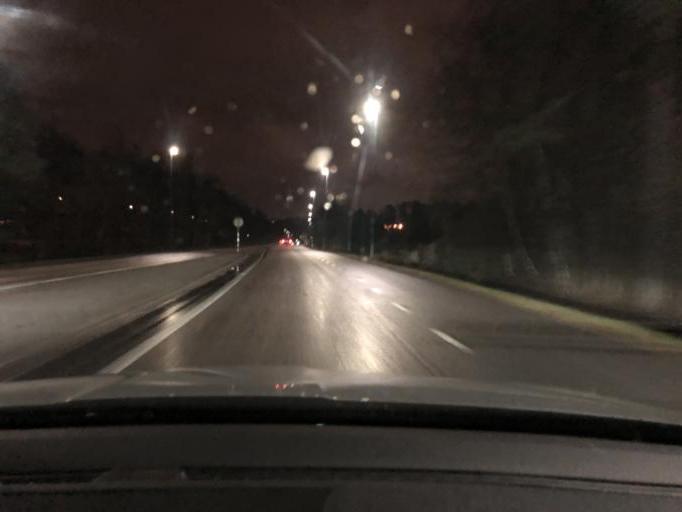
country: SE
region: Stockholm
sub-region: Jarfalla Kommun
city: Jakobsberg
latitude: 59.4028
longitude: 17.8143
